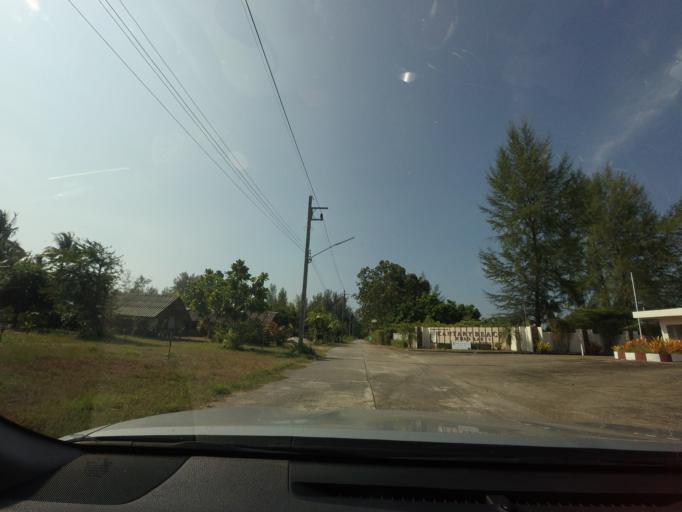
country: TH
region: Phangnga
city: Ban Khao Lak
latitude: 8.7305
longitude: 98.2388
